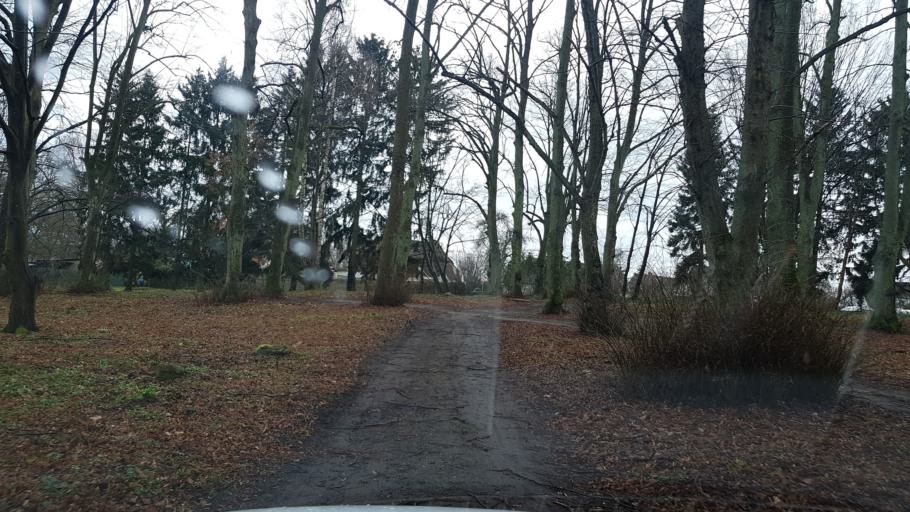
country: PL
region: West Pomeranian Voivodeship
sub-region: Powiat drawski
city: Czaplinek
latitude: 53.5557
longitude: 16.2410
